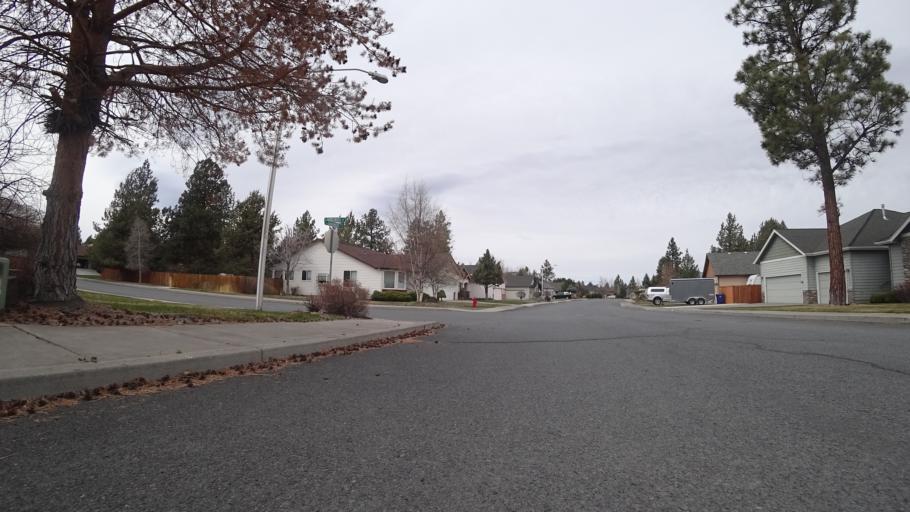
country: US
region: Oregon
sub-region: Deschutes County
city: Bend
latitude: 44.0407
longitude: -121.2754
